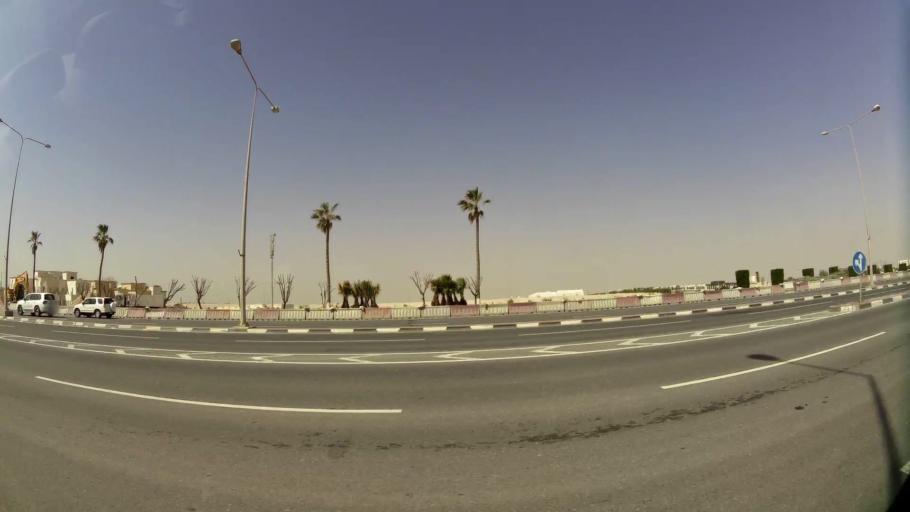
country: QA
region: Baladiyat ad Dawhah
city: Doha
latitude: 25.3571
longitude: 51.4954
